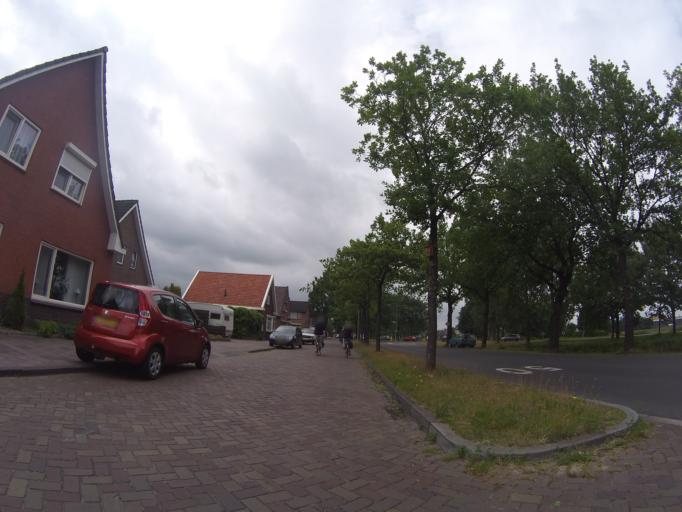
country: NL
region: Drenthe
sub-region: Gemeente Emmen
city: Klazienaveen
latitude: 52.7240
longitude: 7.0045
